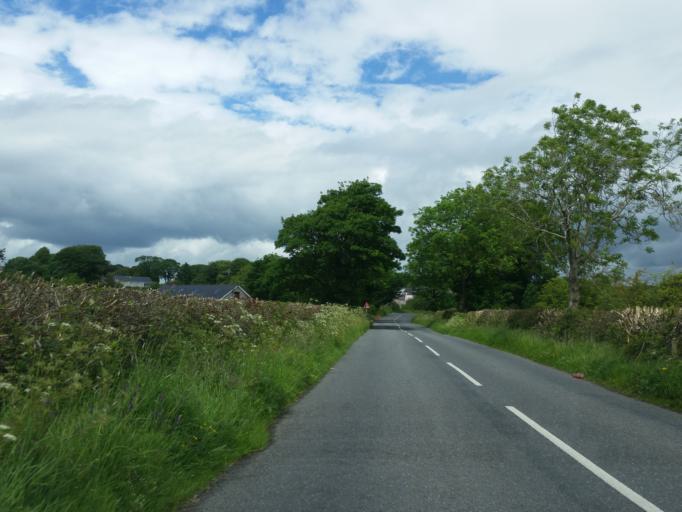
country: GB
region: Northern Ireland
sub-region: Omagh District
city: Omagh
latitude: 54.5518
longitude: -7.1184
